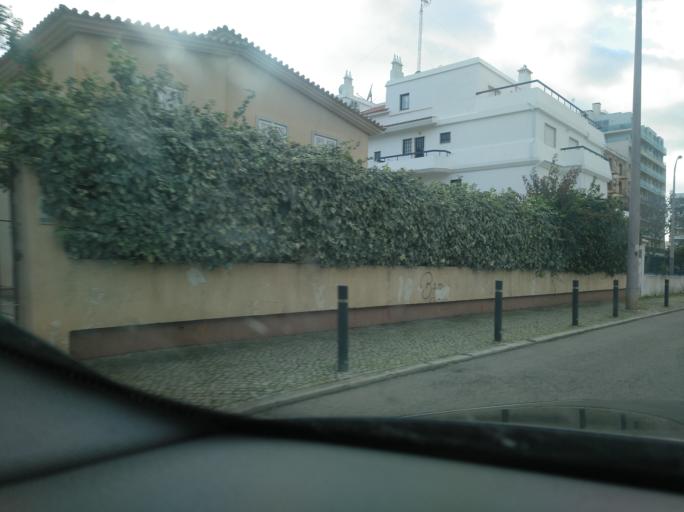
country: PT
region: Faro
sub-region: Vila Real de Santo Antonio
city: Monte Gordo
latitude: 37.1810
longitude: -7.4474
